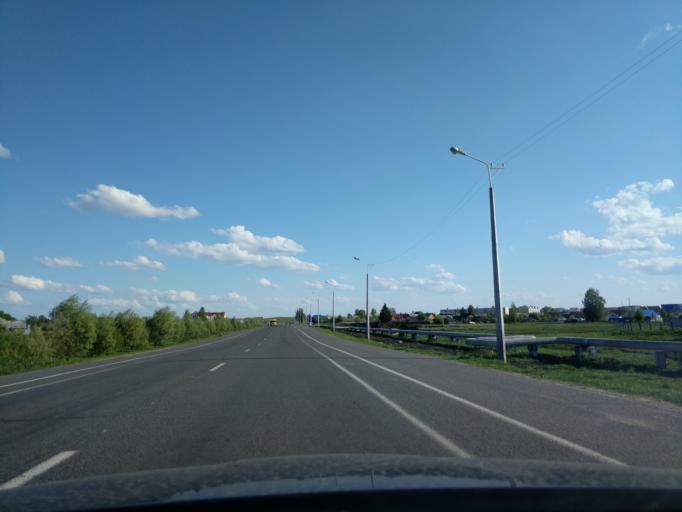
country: BY
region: Minsk
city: Myadzyel
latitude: 54.8810
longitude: 26.9395
